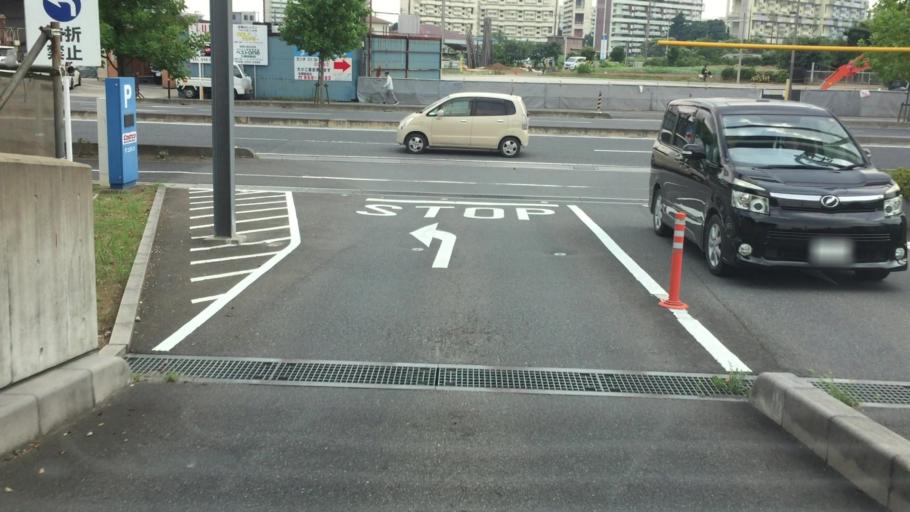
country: JP
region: Saitama
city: Yoshikawa
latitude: 35.8610
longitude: 139.8628
